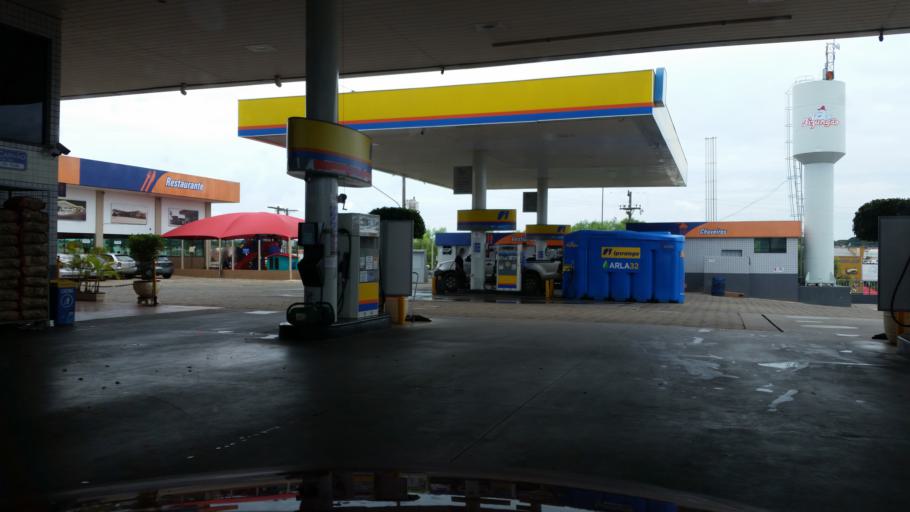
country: BR
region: Sao Paulo
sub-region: Avare
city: Avare
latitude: -23.1058
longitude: -48.9397
